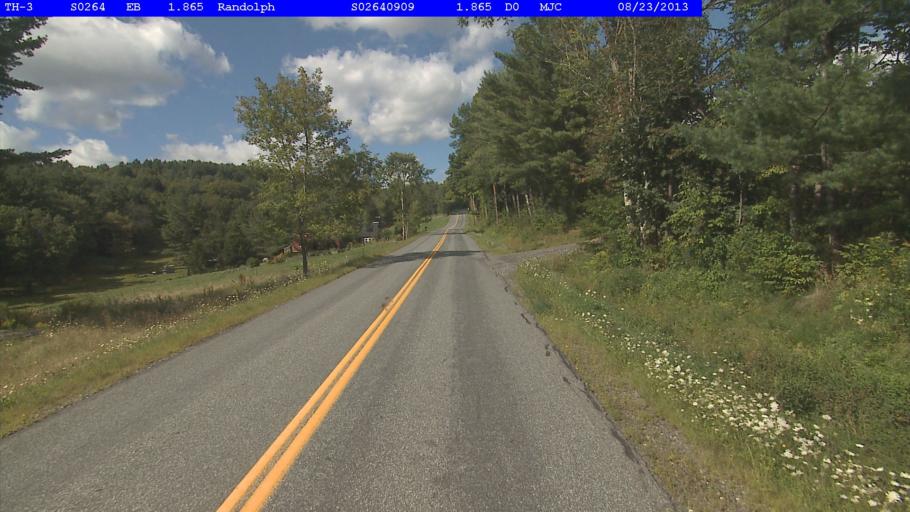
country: US
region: Vermont
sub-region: Orange County
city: Chelsea
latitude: 43.9535
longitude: -72.5325
